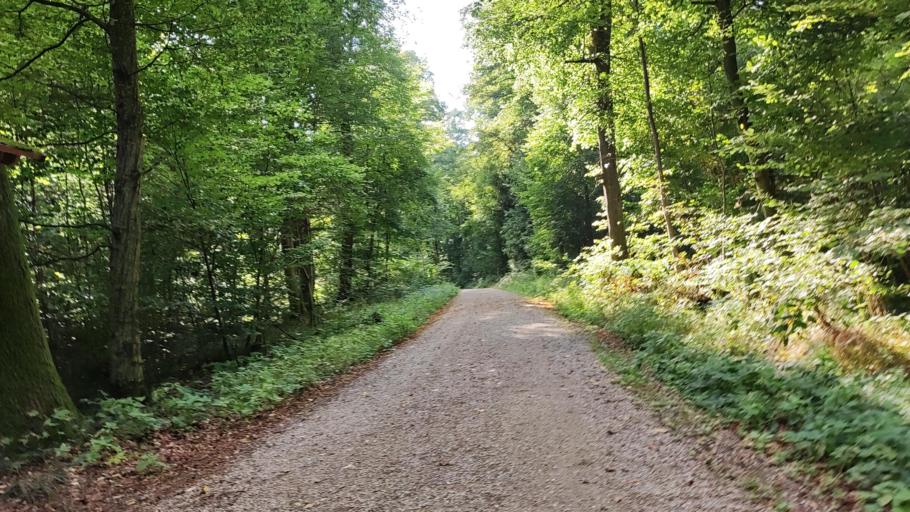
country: DE
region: Bavaria
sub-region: Swabia
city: Zusmarshausen
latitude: 48.3891
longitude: 10.6016
